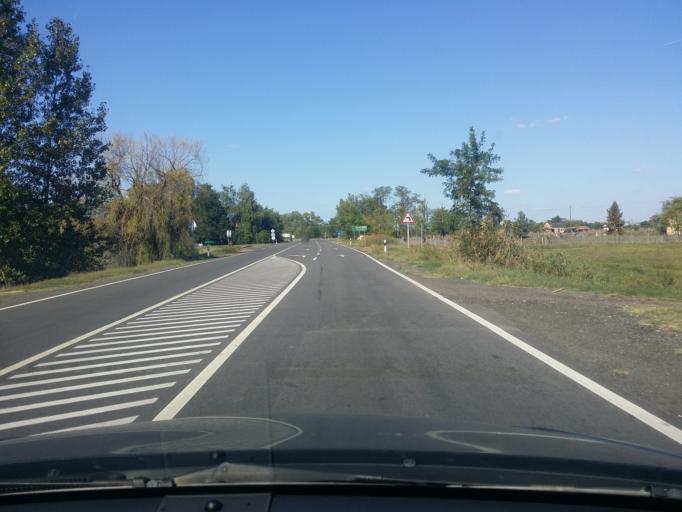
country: HU
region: Bacs-Kiskun
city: Palmonostora
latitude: 46.6352
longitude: 19.8920
